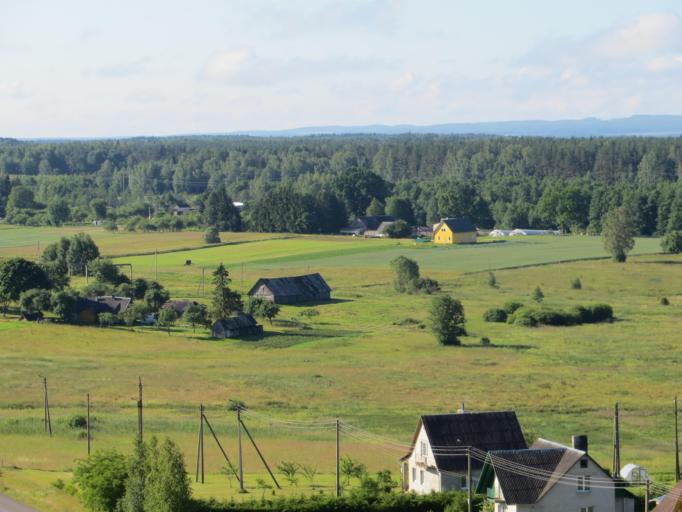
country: LT
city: Pabrade
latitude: 54.9507
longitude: 25.7548
